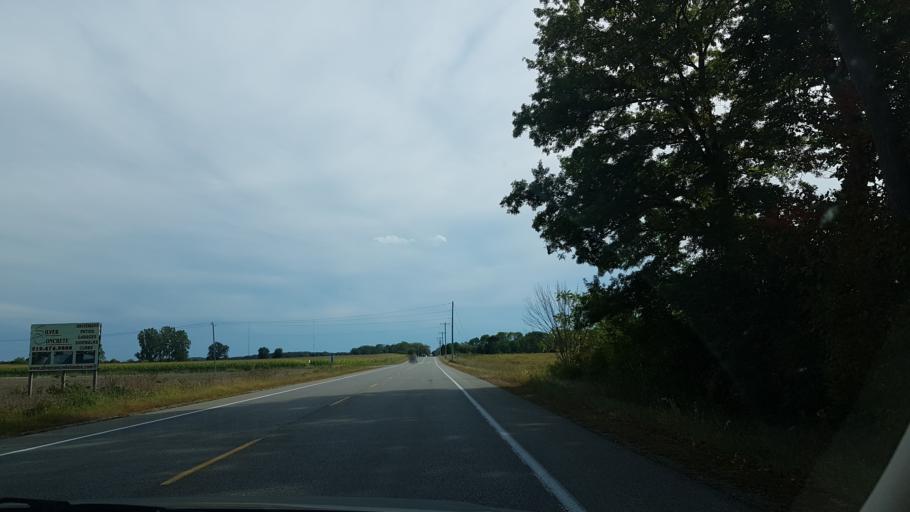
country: CA
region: Ontario
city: Delaware
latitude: 42.9957
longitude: -81.3937
